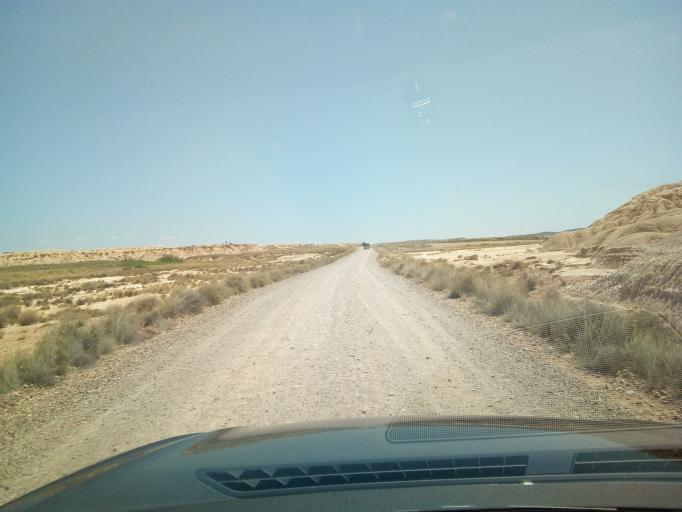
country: ES
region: Navarre
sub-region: Provincia de Navarra
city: Arguedas
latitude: 42.1823
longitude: -1.4705
